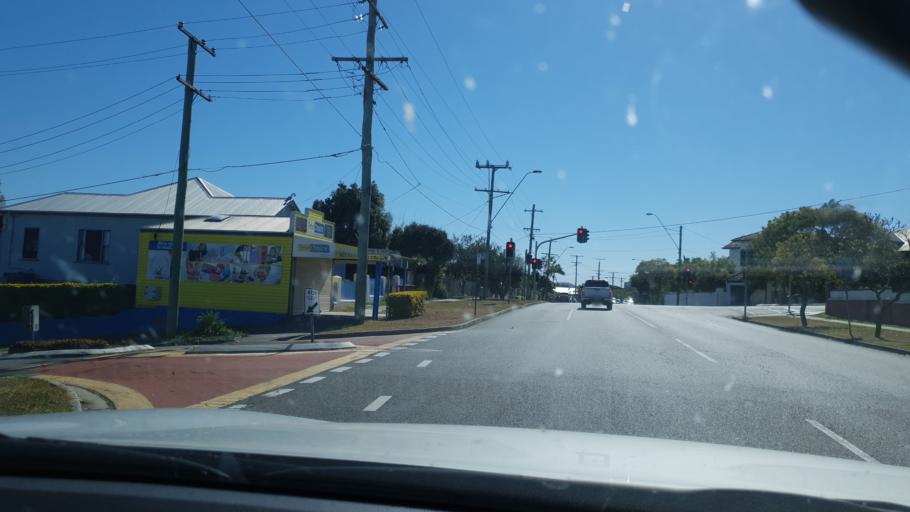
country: AU
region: Queensland
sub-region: Brisbane
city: Annerley
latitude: -27.5032
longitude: 153.0311
